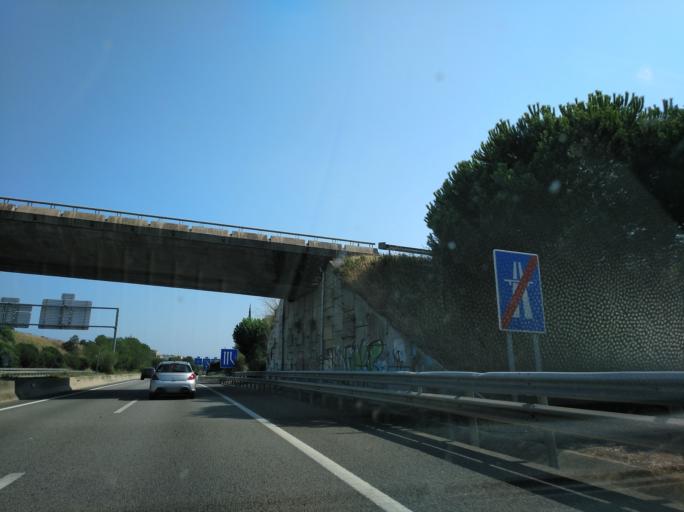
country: ES
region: Catalonia
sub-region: Provincia de Barcelona
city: Argentona
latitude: 41.5520
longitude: 2.4102
